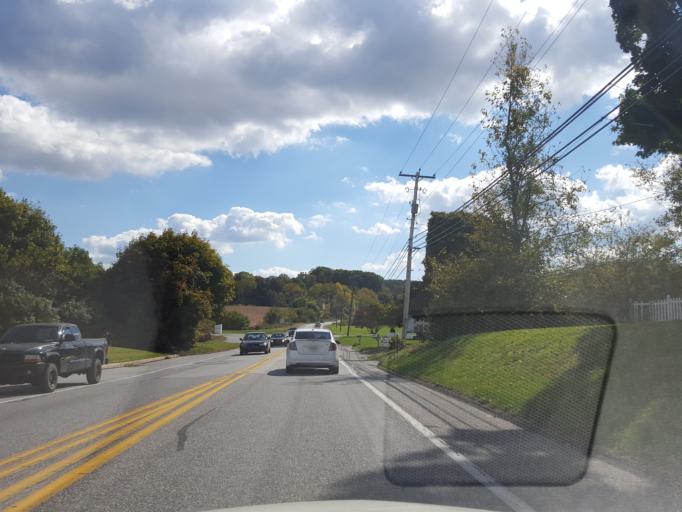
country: US
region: Pennsylvania
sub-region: York County
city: Yoe
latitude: 39.9412
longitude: -76.6450
